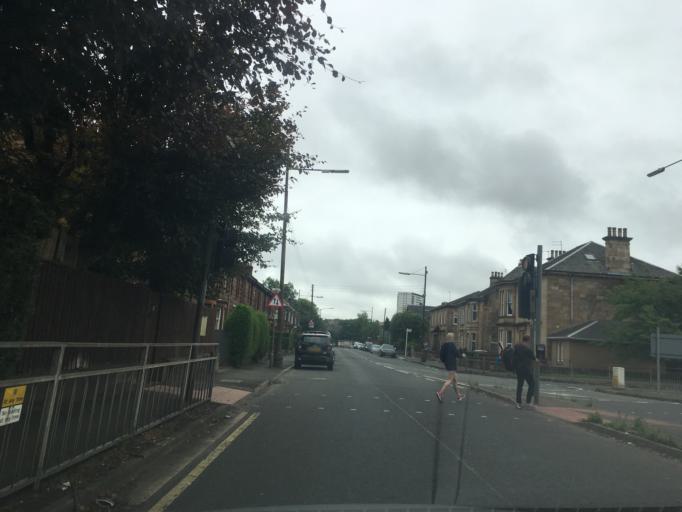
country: GB
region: Scotland
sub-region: East Dunbartonshire
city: Bearsden
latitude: 55.8807
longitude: -4.3258
